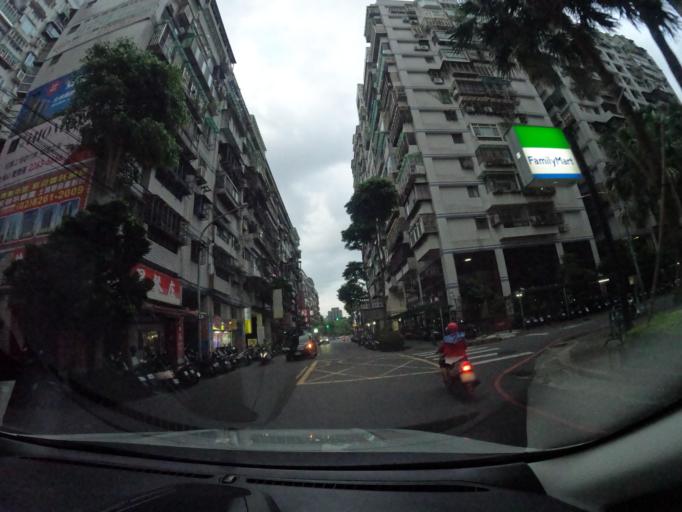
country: TW
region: Taipei
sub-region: Taipei
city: Banqiao
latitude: 24.9817
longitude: 121.4491
